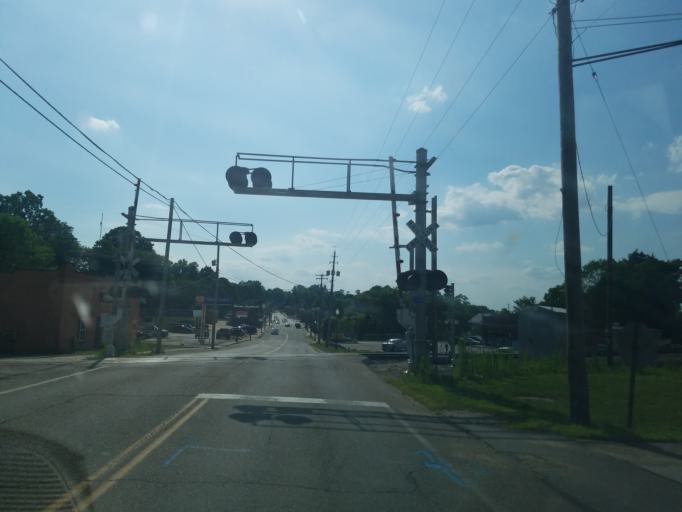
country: US
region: Ohio
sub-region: Summit County
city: Mogadore
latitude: 41.0510
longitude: -81.3905
